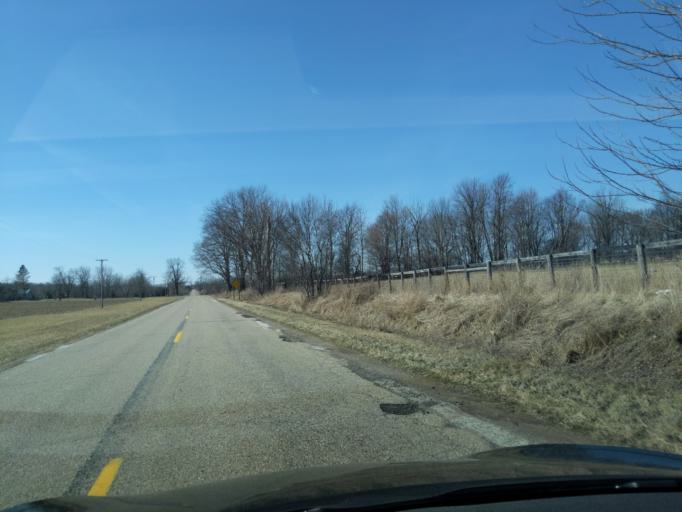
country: US
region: Michigan
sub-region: Ionia County
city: Portland
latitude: 42.7267
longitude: -84.9527
